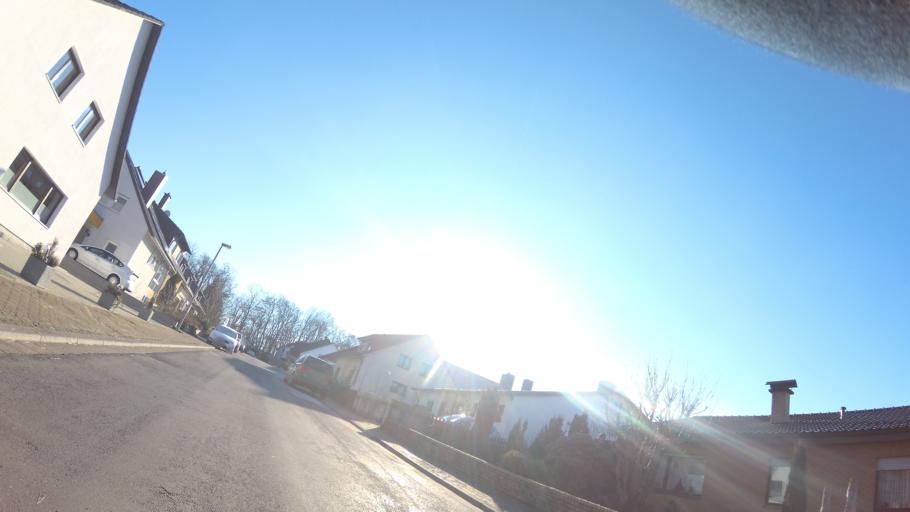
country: DE
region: Saarland
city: Wallerfangen
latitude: 49.3110
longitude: 6.7197
